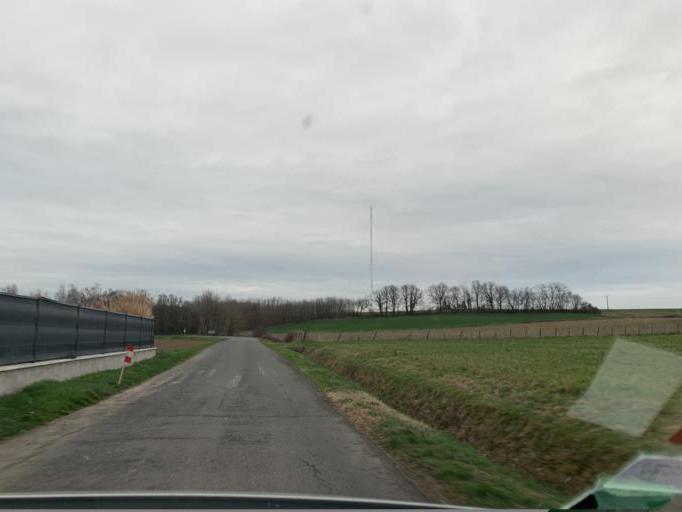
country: FR
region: Rhone-Alpes
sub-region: Departement de l'Ain
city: Mionnay
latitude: 45.8740
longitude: 4.9382
